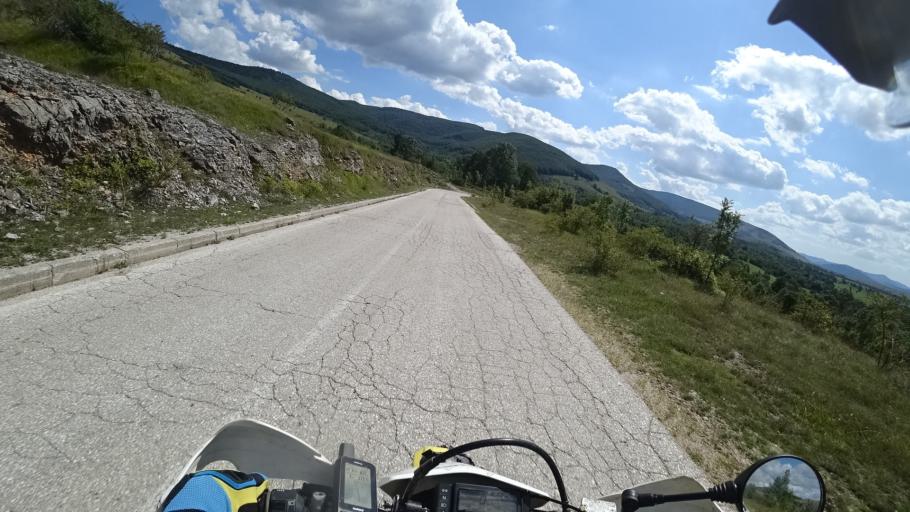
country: BA
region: Federation of Bosnia and Herzegovina
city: Orasac
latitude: 44.4669
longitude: 15.9799
